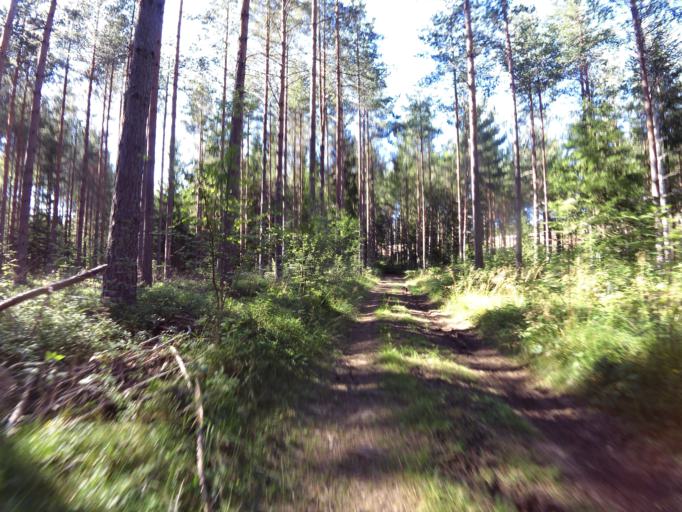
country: SE
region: Gaevleborg
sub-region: Hofors Kommun
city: Hofors
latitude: 60.5855
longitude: 16.3941
